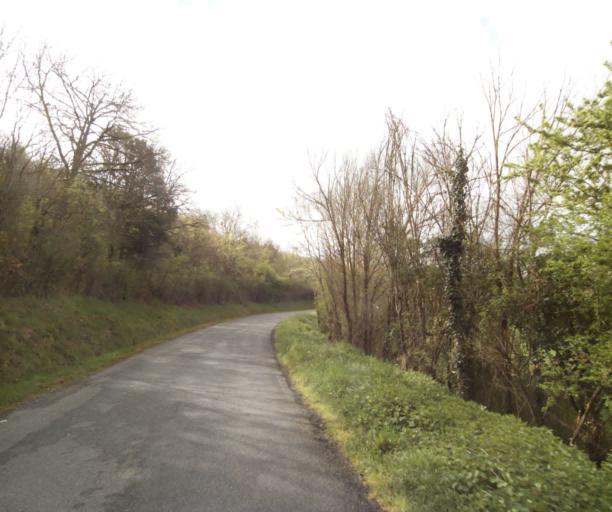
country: FR
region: Midi-Pyrenees
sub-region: Departement de l'Ariege
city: Saverdun
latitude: 43.2369
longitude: 1.5629
